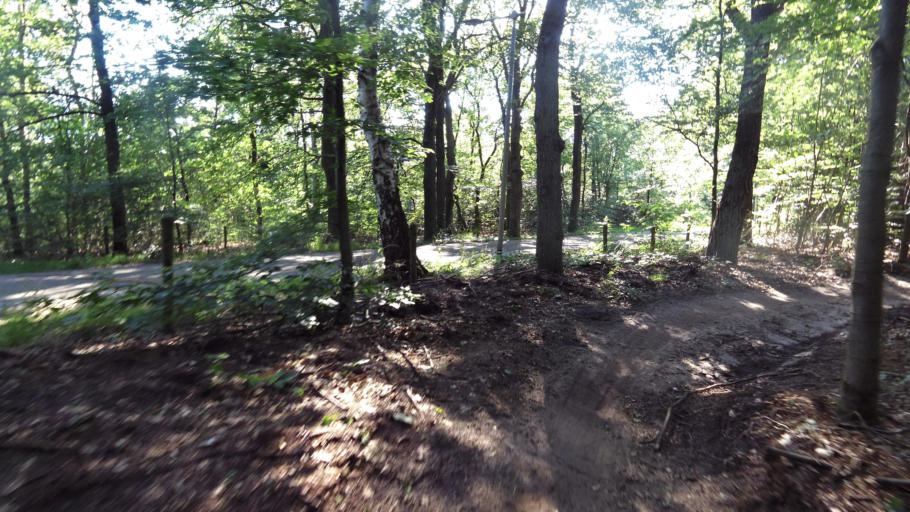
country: NL
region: Gelderland
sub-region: Gemeente Renkum
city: Oosterbeek
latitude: 52.0175
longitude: 5.8263
